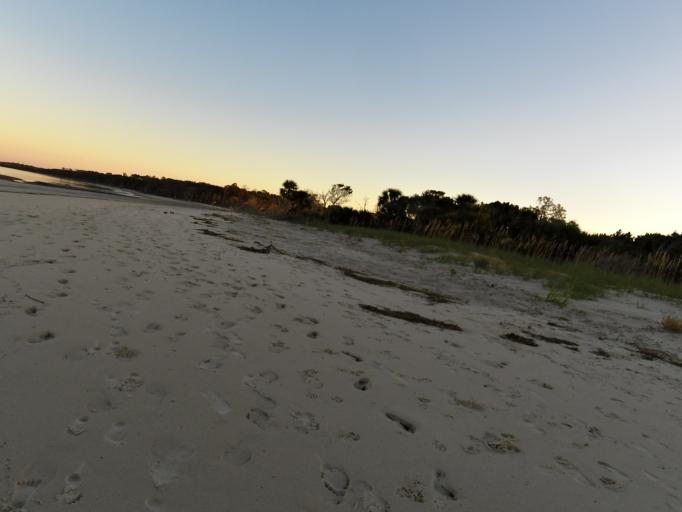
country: US
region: Florida
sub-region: Nassau County
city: Fernandina Beach
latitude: 30.5103
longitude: -81.4555
